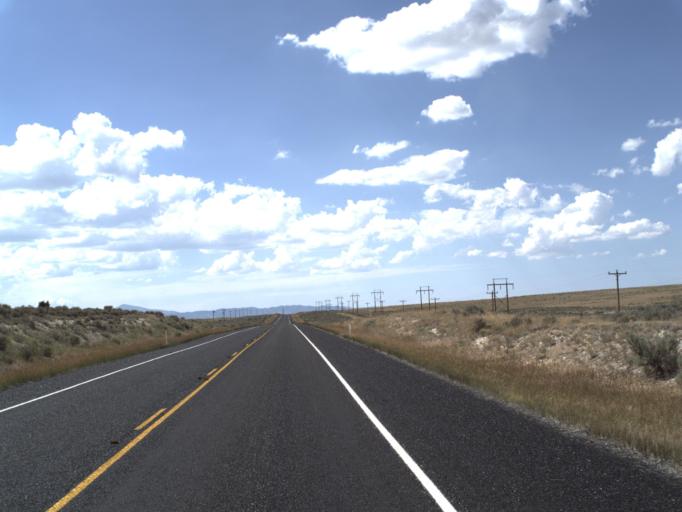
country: US
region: Idaho
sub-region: Minidoka County
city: Rupert
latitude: 41.9832
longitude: -113.1718
